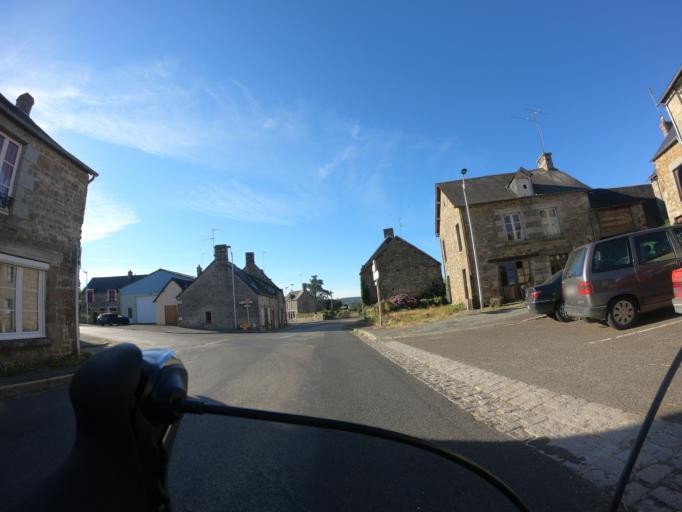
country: FR
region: Pays de la Loire
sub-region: Departement de la Mayenne
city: Pre-en-Pail
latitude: 48.5420
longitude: -0.2064
